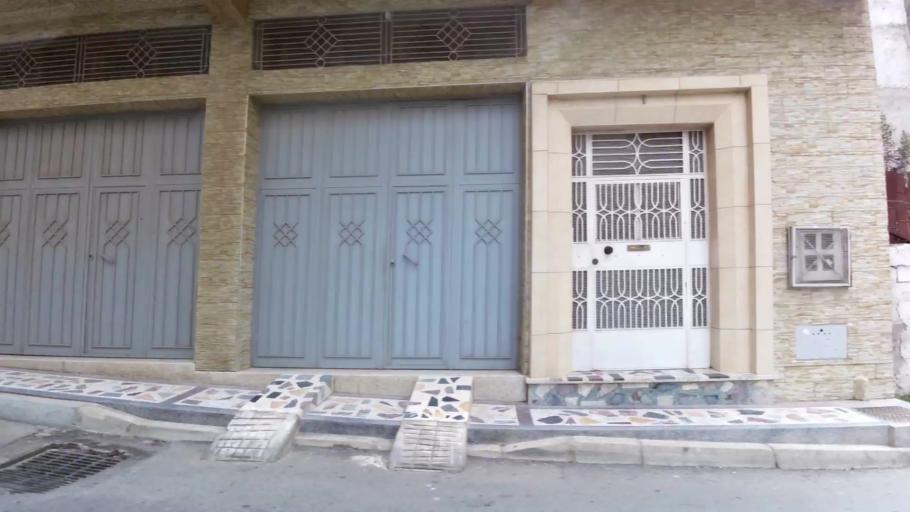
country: MA
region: Tanger-Tetouan
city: Tetouan
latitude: 35.5667
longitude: -5.3961
